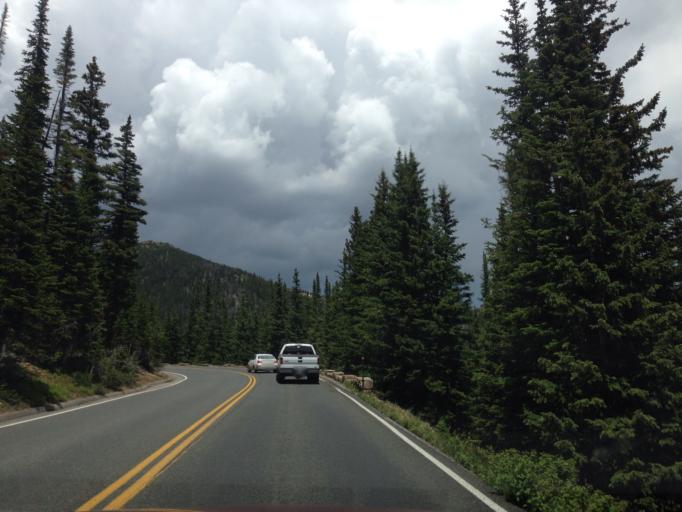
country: US
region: Colorado
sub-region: Larimer County
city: Estes Park
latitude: 40.3866
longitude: -105.6678
